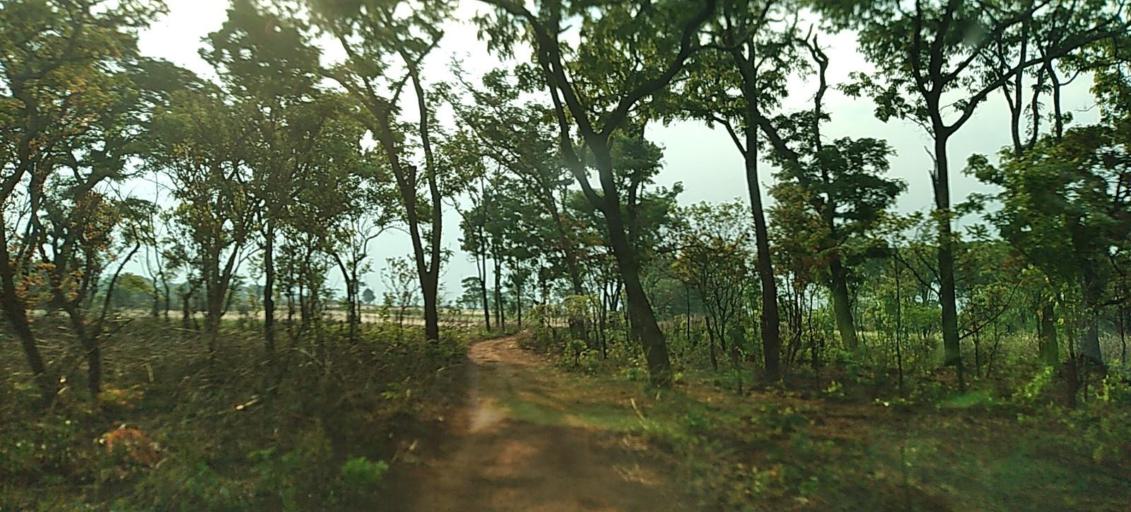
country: ZM
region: North-Western
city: Solwezi
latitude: -12.0463
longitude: 26.0602
